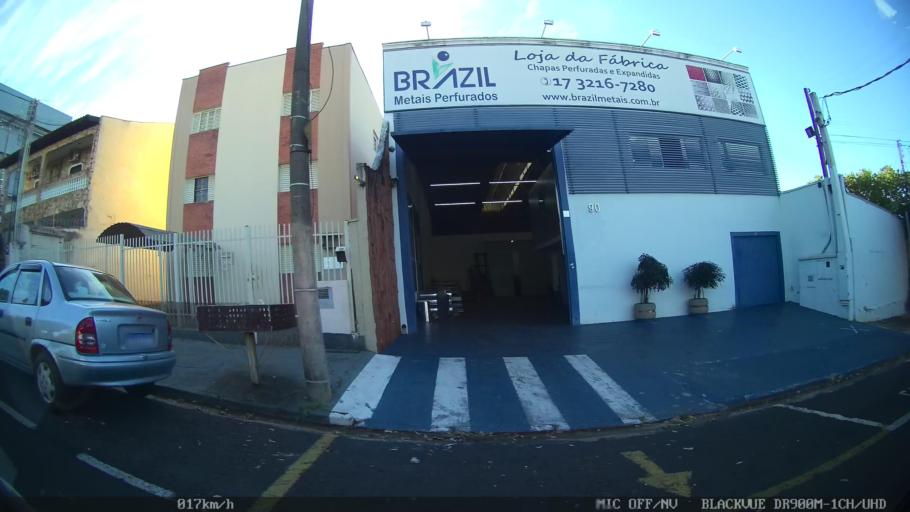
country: BR
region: Sao Paulo
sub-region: Sao Jose Do Rio Preto
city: Sao Jose do Rio Preto
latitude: -20.8257
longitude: -49.3687
